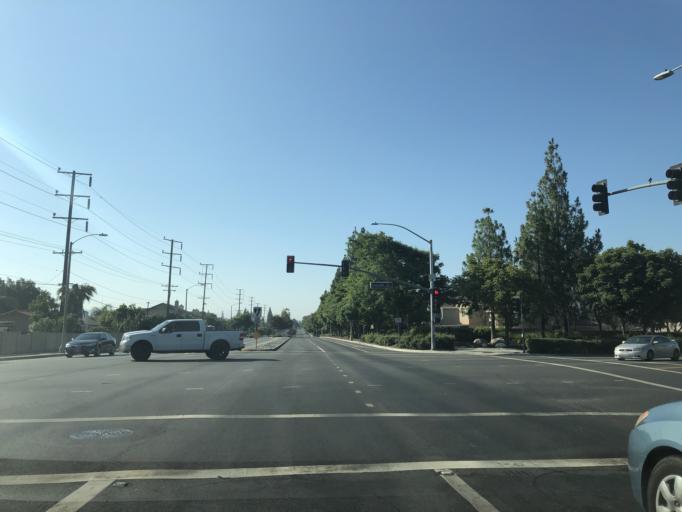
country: US
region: California
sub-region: Riverside County
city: Corona
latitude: 33.8996
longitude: -117.5750
